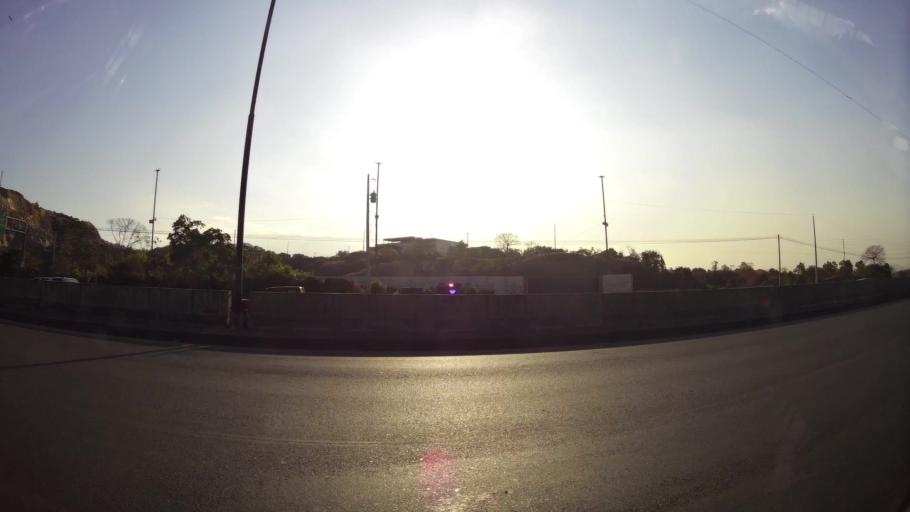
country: EC
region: Guayas
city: Santa Lucia
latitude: -2.1511
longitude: -79.9463
